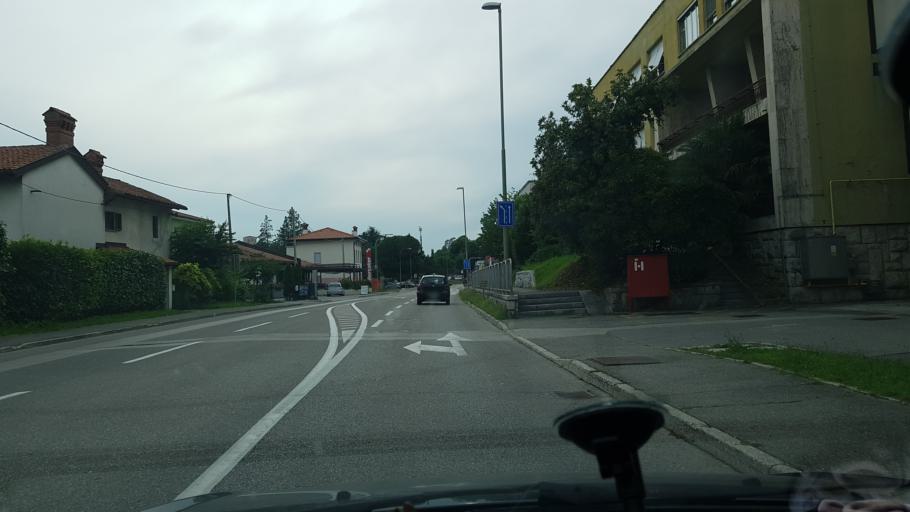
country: SI
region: Sempeter-Vrtojba
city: Sempeter pri Gorici
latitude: 45.9422
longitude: 13.6406
